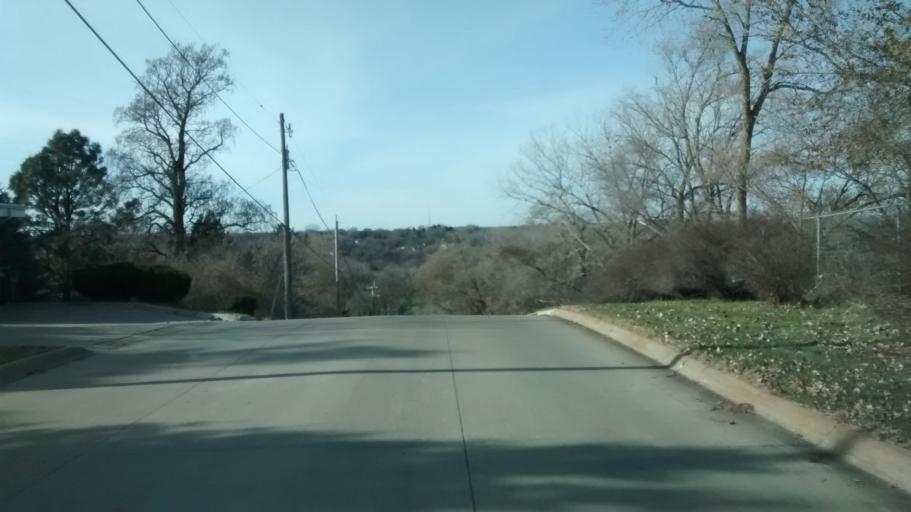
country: US
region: Iowa
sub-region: Woodbury County
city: Sioux City
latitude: 42.5375
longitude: -96.4030
